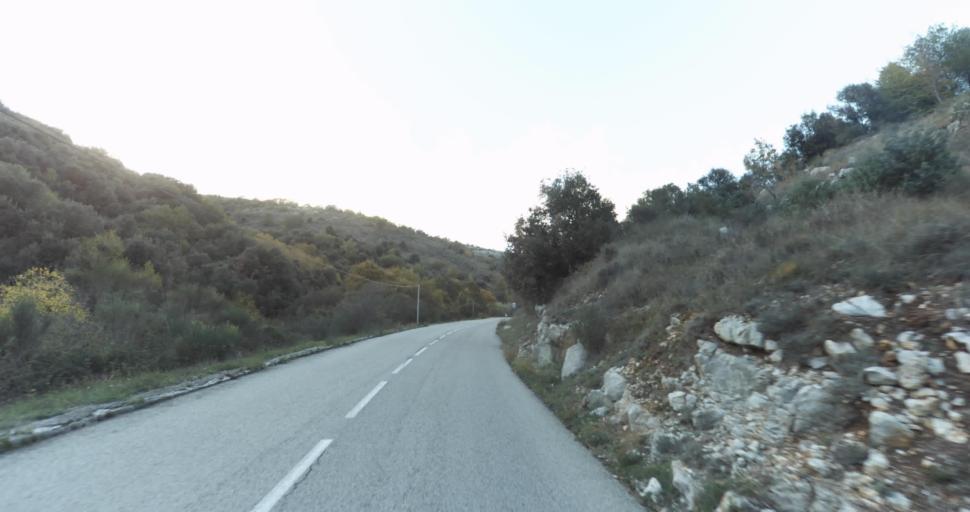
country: FR
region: Provence-Alpes-Cote d'Azur
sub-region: Departement des Alpes-Maritimes
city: Vence
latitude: 43.7478
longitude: 7.0977
